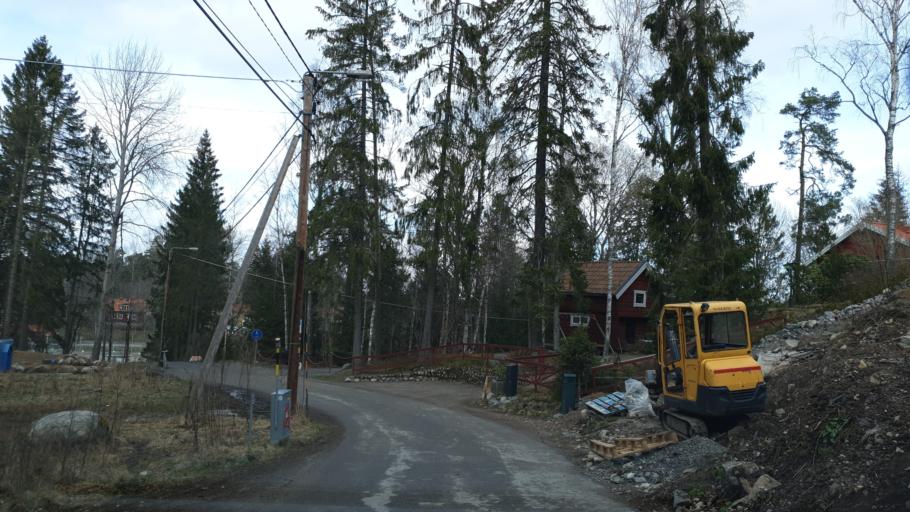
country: SE
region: Stockholm
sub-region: Nacka Kommun
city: Boo
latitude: 59.3325
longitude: 18.2906
